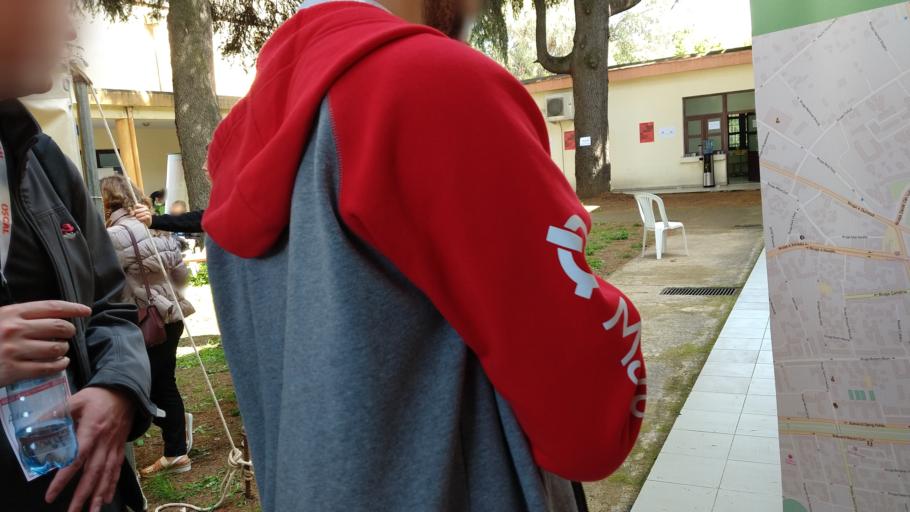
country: AL
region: Tirane
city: Tirana
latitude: 41.3353
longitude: 19.8073
